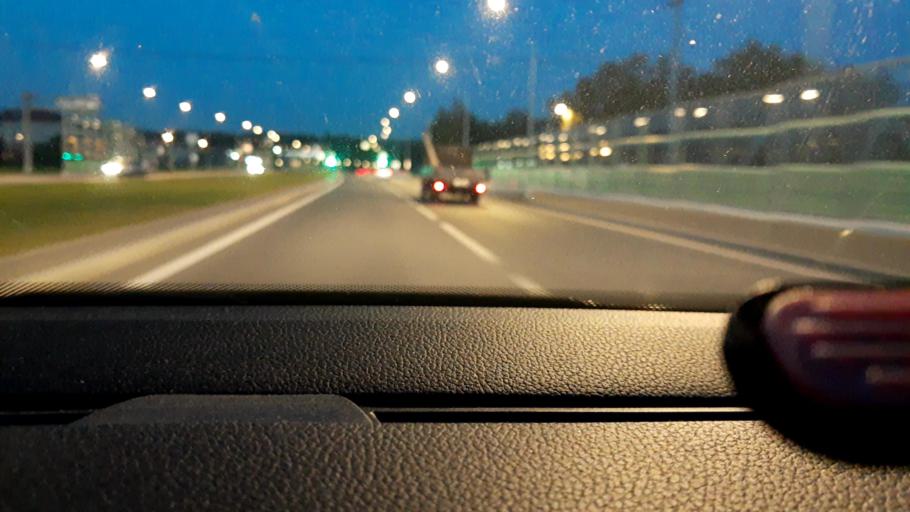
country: RU
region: Moskovskaya
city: Filimonki
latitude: 55.5625
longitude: 37.3420
